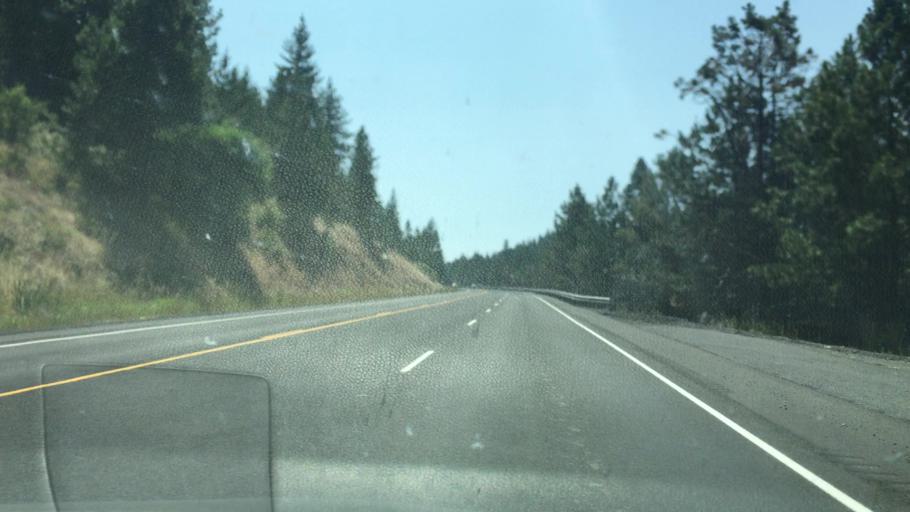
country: US
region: Idaho
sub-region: Idaho County
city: Grangeville
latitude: 45.8654
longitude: -116.2366
